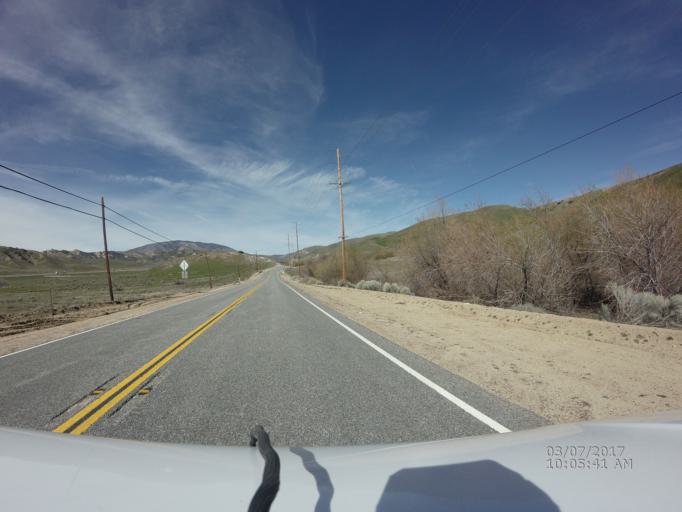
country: US
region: California
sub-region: Kern County
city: Lebec
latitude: 34.7832
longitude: -118.8111
